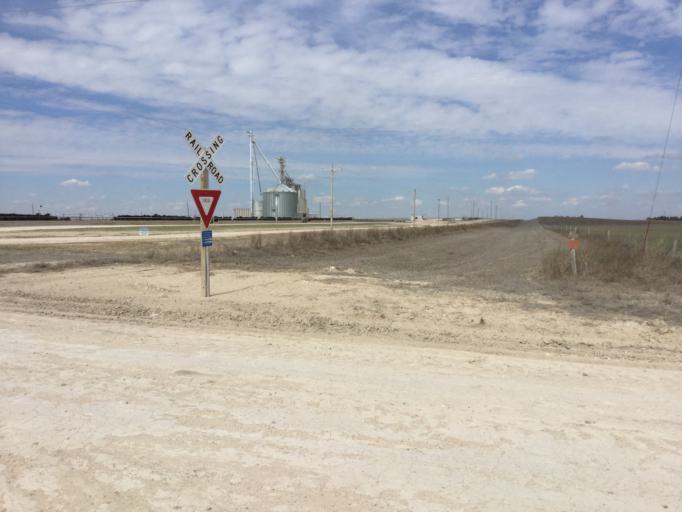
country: US
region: Kansas
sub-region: Scott County
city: Scott City
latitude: 38.3229
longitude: -100.9145
